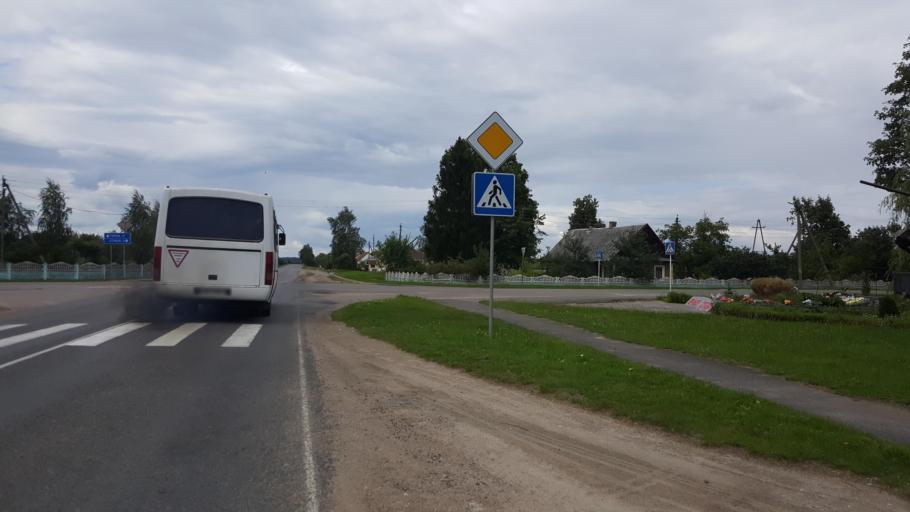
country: BY
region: Brest
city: Kamyanyets
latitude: 52.3166
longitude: 23.9200
